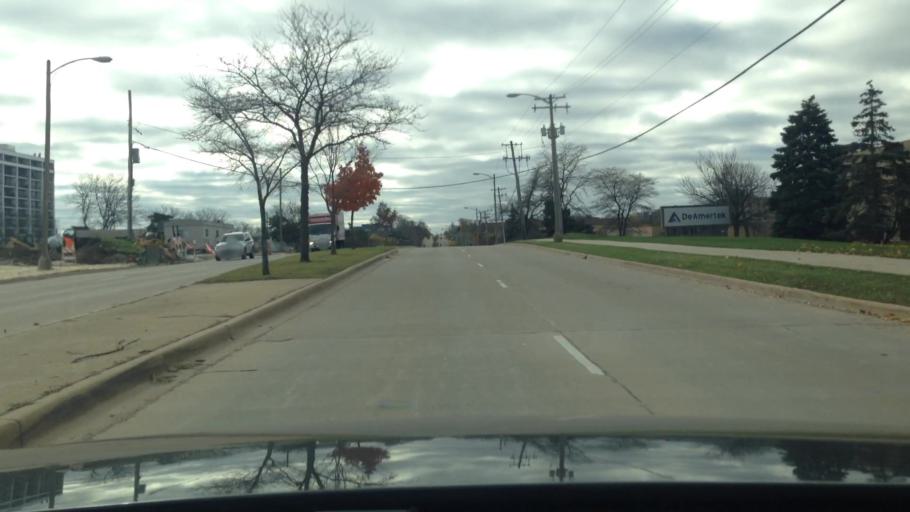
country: US
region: Illinois
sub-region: DuPage County
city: Lombard
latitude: 41.8493
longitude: -88.0266
